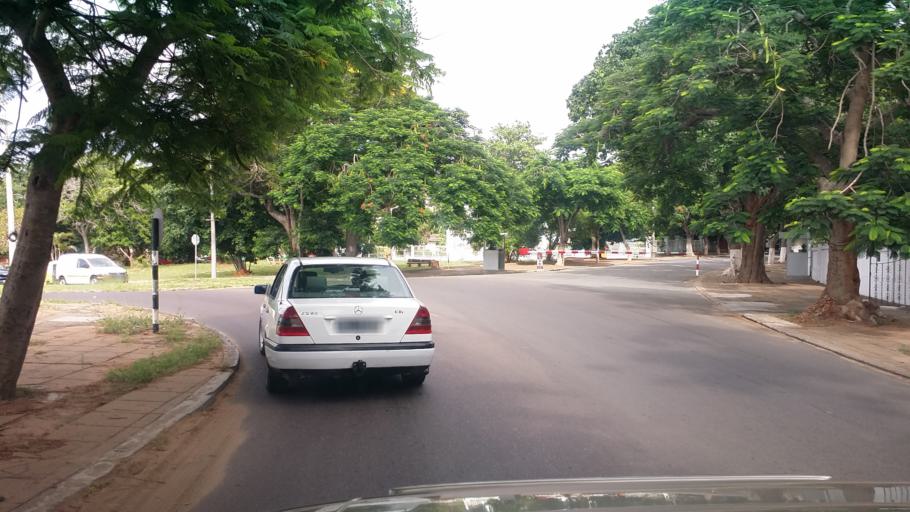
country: MZ
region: Maputo City
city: Maputo
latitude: -25.9815
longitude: 32.5916
